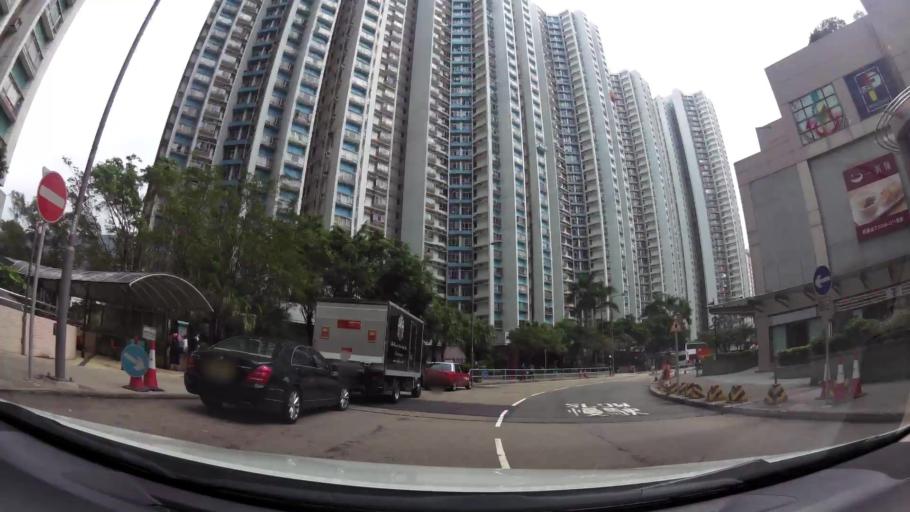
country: HK
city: Yung Shue Wan
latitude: 22.2441
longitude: 114.1460
